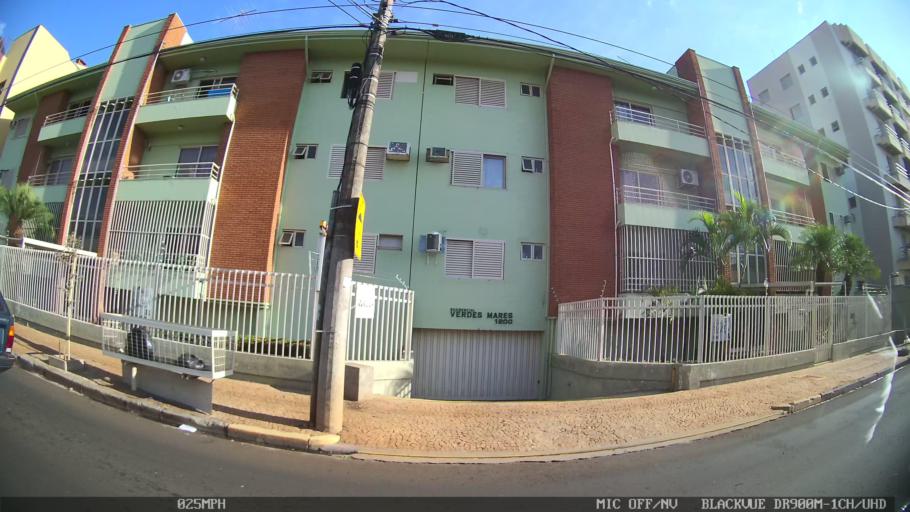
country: BR
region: Sao Paulo
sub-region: Ribeirao Preto
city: Ribeirao Preto
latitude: -21.1932
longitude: -47.7840
